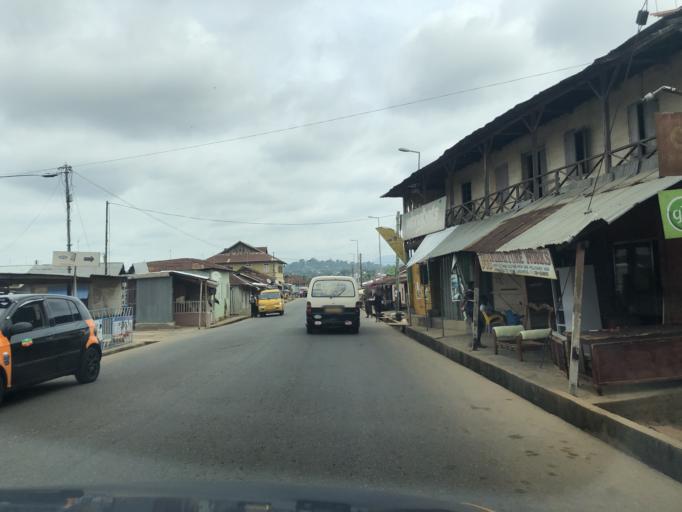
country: GH
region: Eastern
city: Koforidua
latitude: 6.1089
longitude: -0.2681
